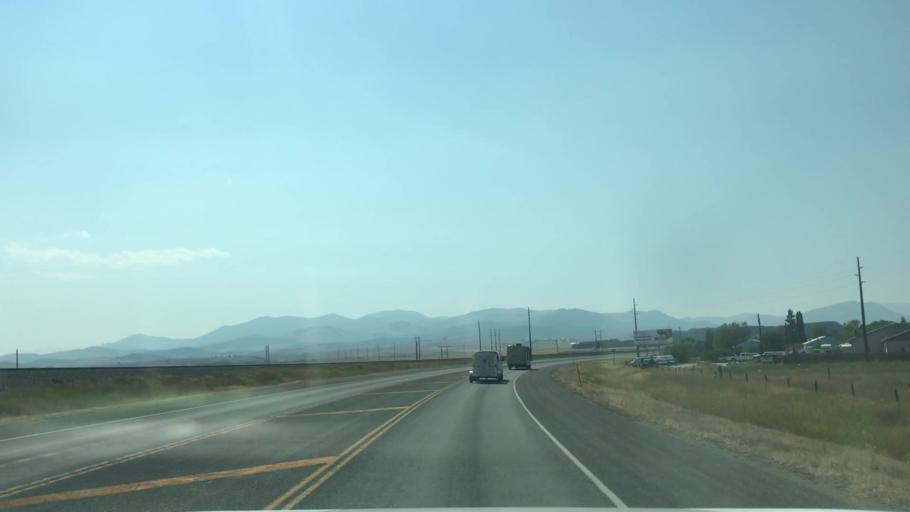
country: US
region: Montana
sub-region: Lewis and Clark County
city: East Helena
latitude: 46.5867
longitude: -111.8954
